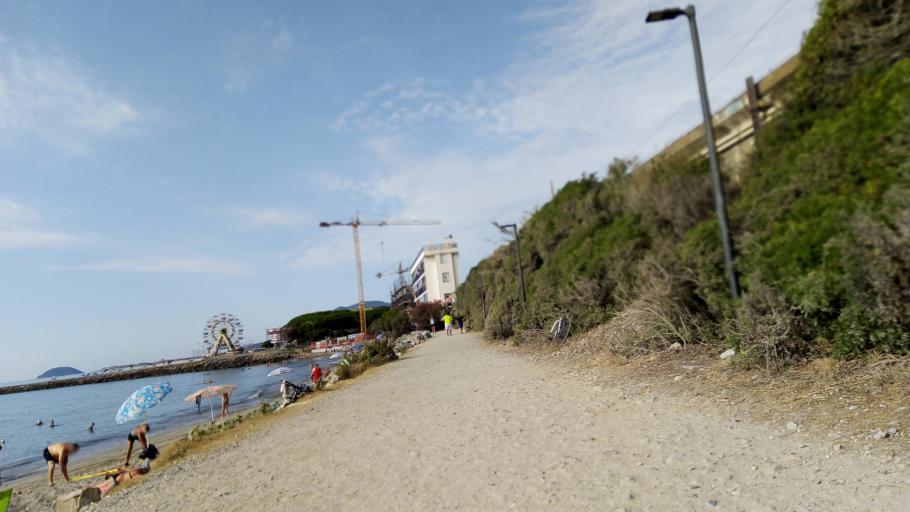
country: IT
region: Liguria
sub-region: Provincia di Savona
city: Borghetto Santo Spirito
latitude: 44.1019
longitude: 8.2373
